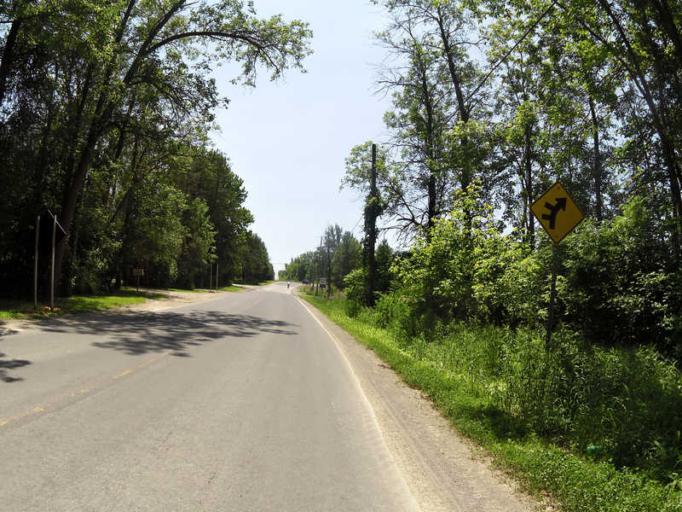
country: CA
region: Ontario
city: Peterborough
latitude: 44.3879
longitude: -78.2696
